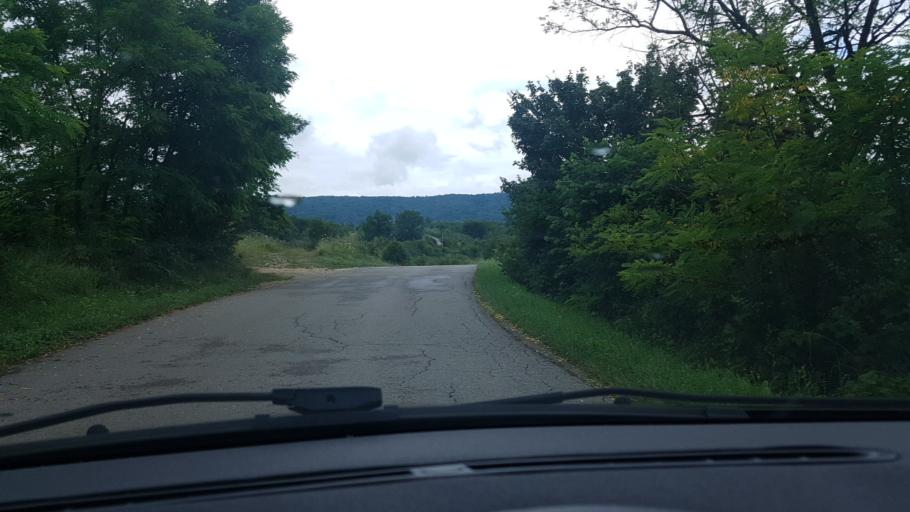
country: BA
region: Federation of Bosnia and Herzegovina
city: Trzacka Rastela
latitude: 44.9842
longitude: 15.7283
